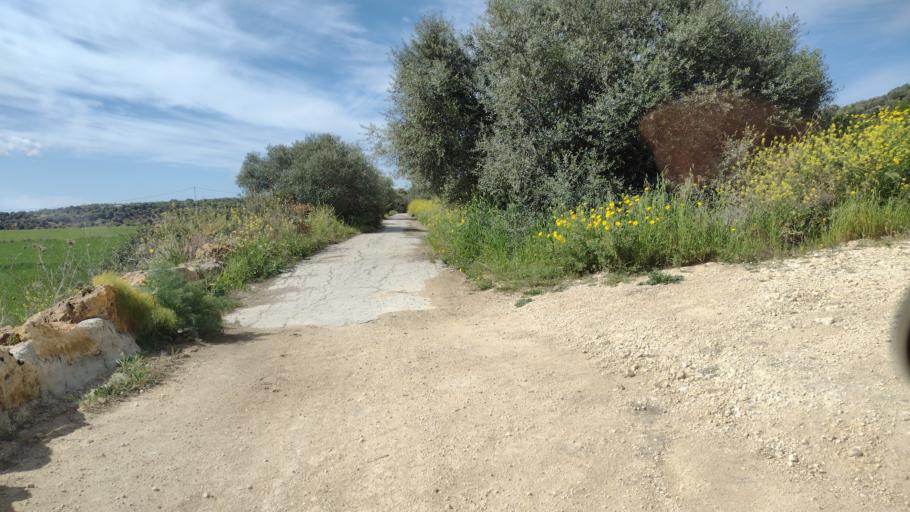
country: IT
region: Sicily
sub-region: Provincia di Siracusa
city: Noto
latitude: 36.9021
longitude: 15.0157
